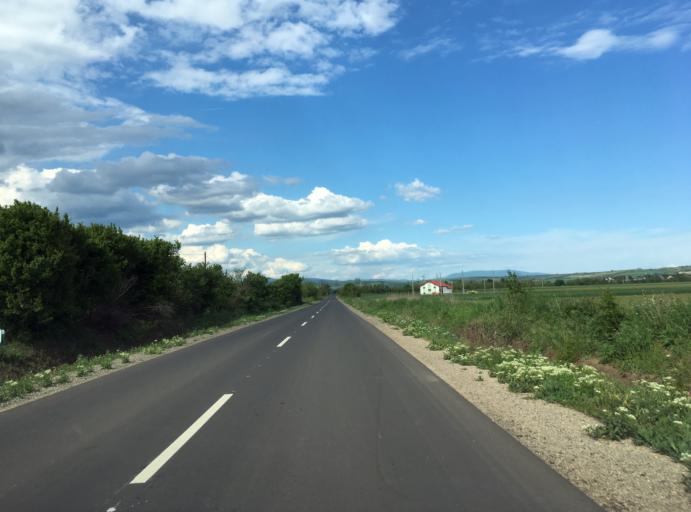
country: HU
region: Heves
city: Hered
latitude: 47.7192
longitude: 19.6480
